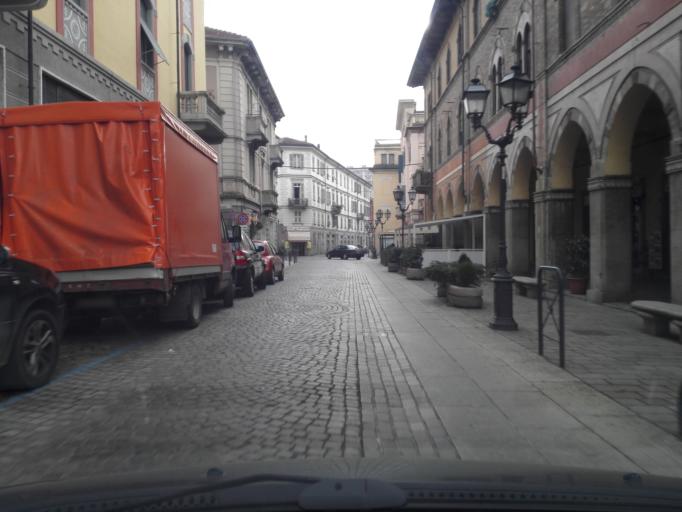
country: IT
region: Piedmont
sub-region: Provincia di Alessandria
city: Alessandria
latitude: 44.9167
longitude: 8.6109
